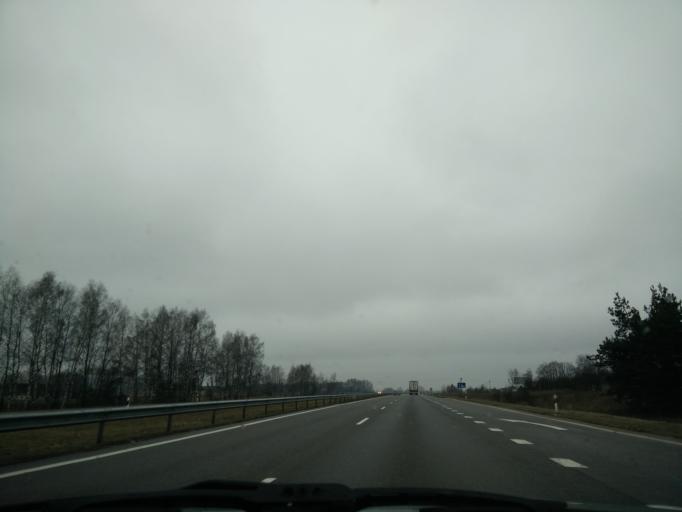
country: LT
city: Skaudvile
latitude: 55.3996
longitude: 22.8596
